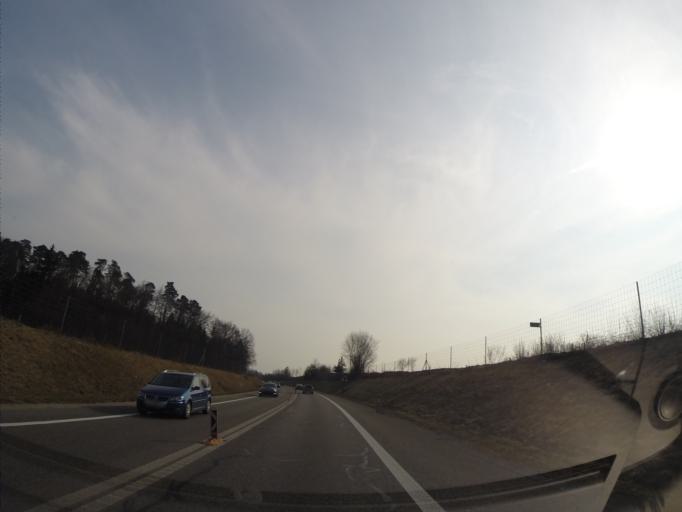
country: CH
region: Zurich
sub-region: Bezirk Andelfingen
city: Henggart
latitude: 47.5675
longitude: 8.6881
